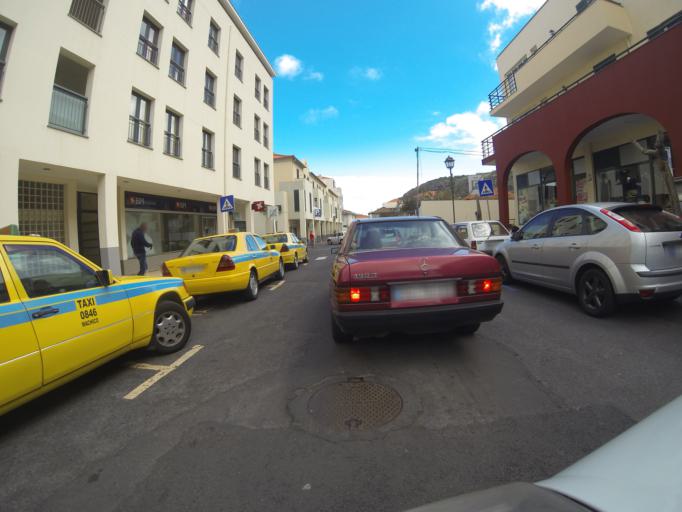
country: PT
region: Madeira
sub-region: Machico
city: Machico
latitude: 32.7191
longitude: -16.7668
